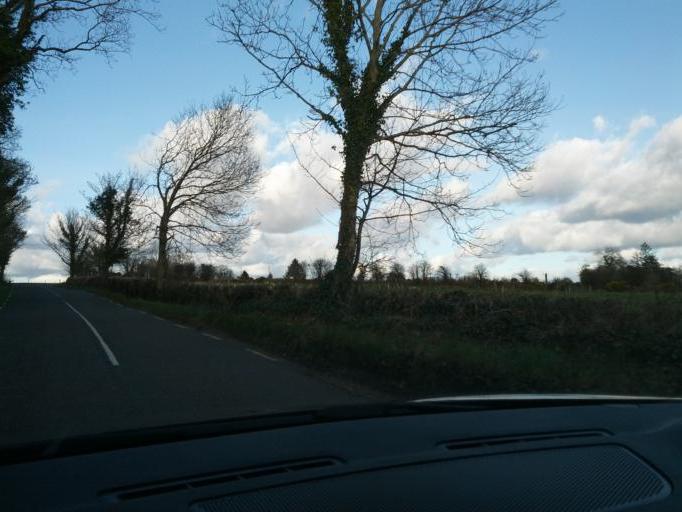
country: IE
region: Connaught
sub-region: Roscommon
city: Castlerea
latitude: 53.5271
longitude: -8.5687
